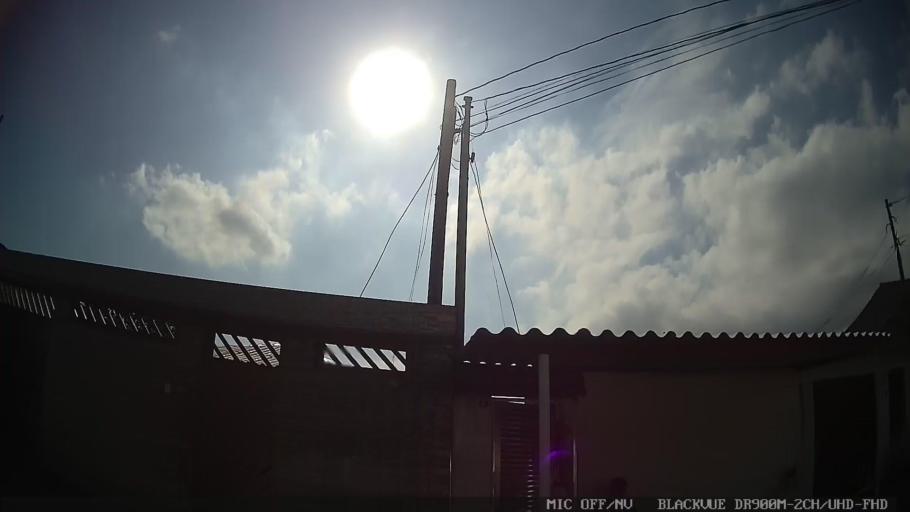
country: BR
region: Sao Paulo
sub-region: Santos
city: Santos
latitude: -23.9459
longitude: -46.3035
